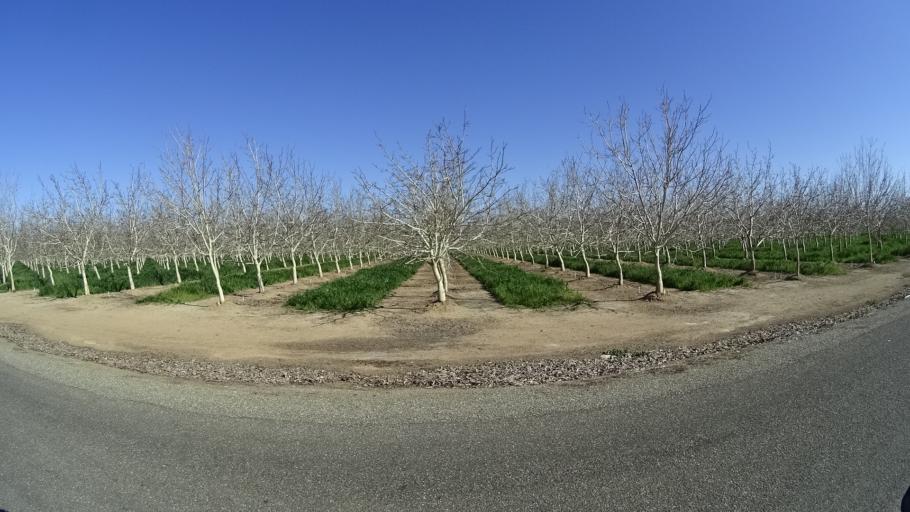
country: US
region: California
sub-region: Glenn County
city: Orland
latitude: 39.7370
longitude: -122.2451
